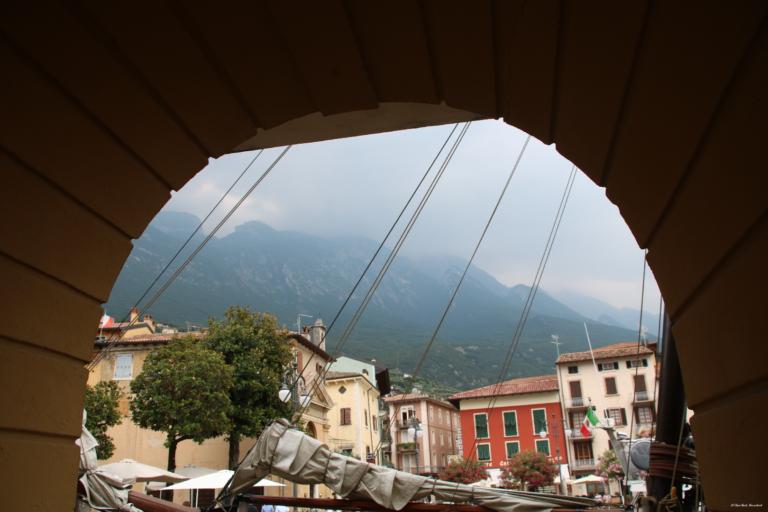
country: IT
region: Veneto
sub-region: Provincia di Verona
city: Malcesine
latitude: 45.7639
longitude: 10.8073
